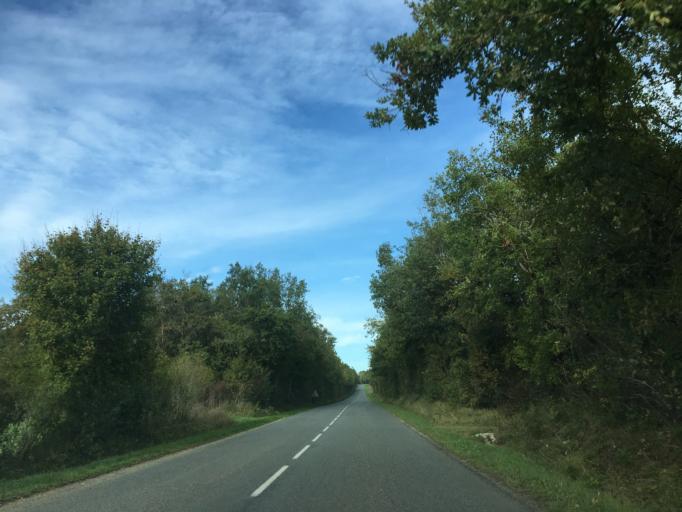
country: FR
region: Poitou-Charentes
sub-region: Departement de la Charente-Maritime
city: Aulnay
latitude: 46.0545
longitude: -0.4041
